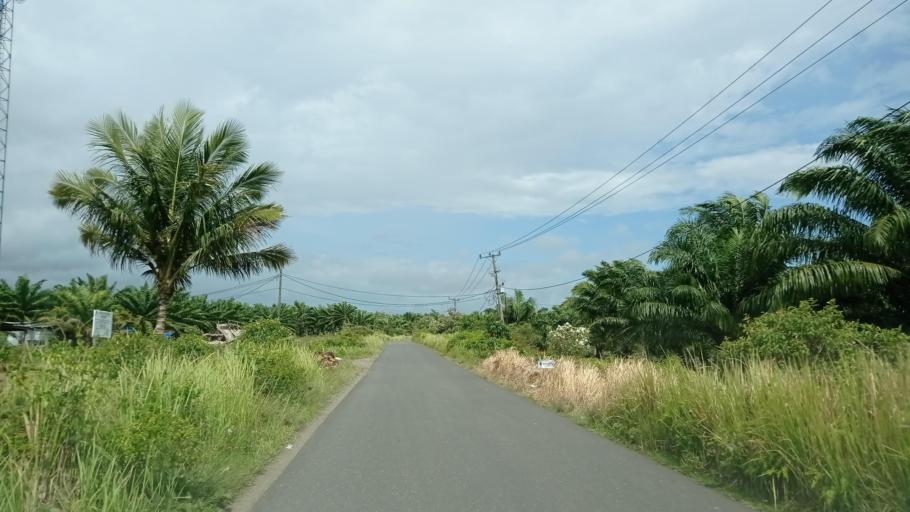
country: ID
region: Jambi
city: Sungai Penuh
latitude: -2.5527
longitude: 101.1079
